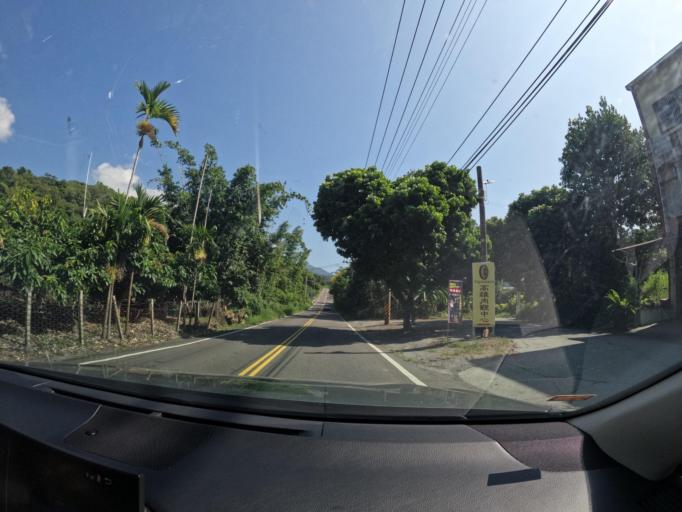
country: TW
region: Taiwan
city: Yujing
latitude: 23.0876
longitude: 120.6809
